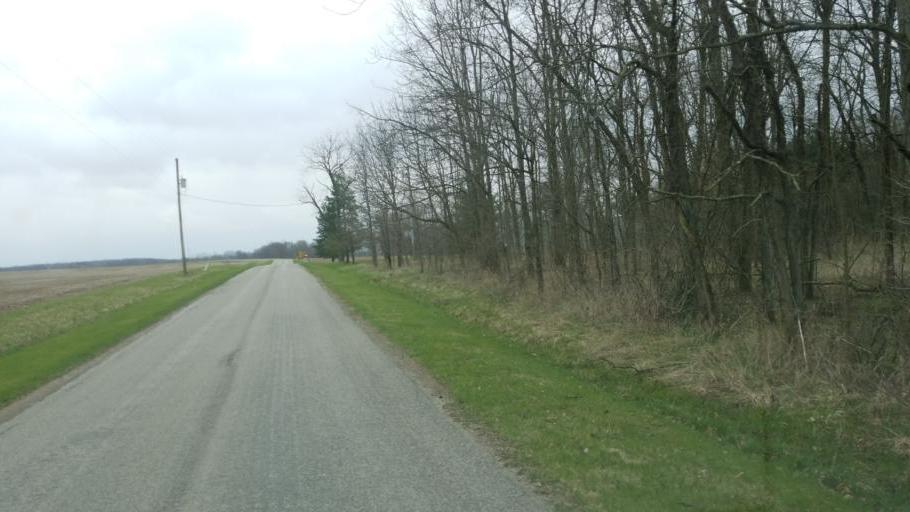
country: US
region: Ohio
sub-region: Union County
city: Richwood
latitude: 40.4207
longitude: -83.3703
